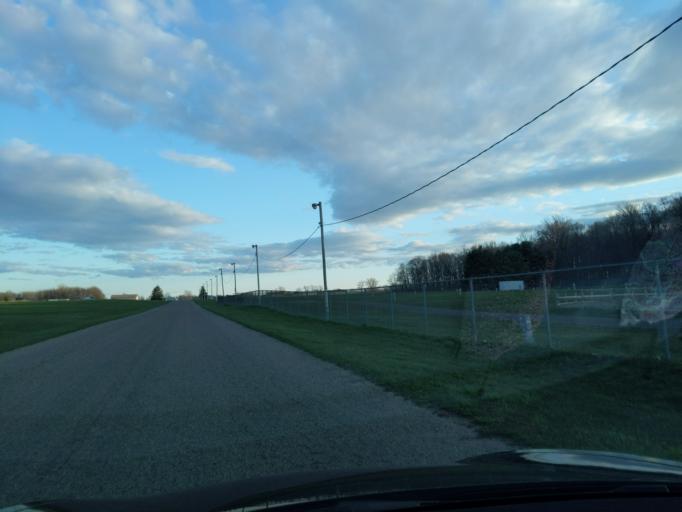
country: US
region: Michigan
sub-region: Ingham County
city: Mason
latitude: 42.5710
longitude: -84.4284
